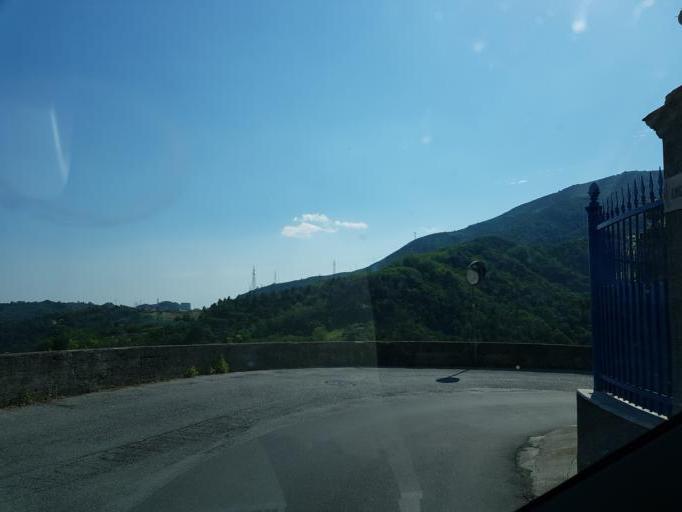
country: IT
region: Liguria
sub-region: Provincia di Genova
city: Genoa
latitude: 44.4579
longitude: 8.8899
